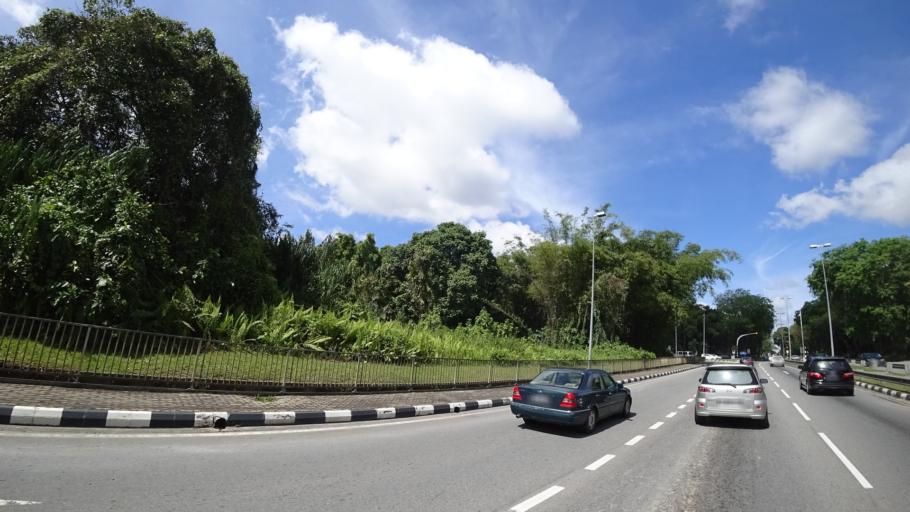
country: BN
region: Brunei and Muara
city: Bandar Seri Begawan
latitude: 4.8631
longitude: 114.9007
